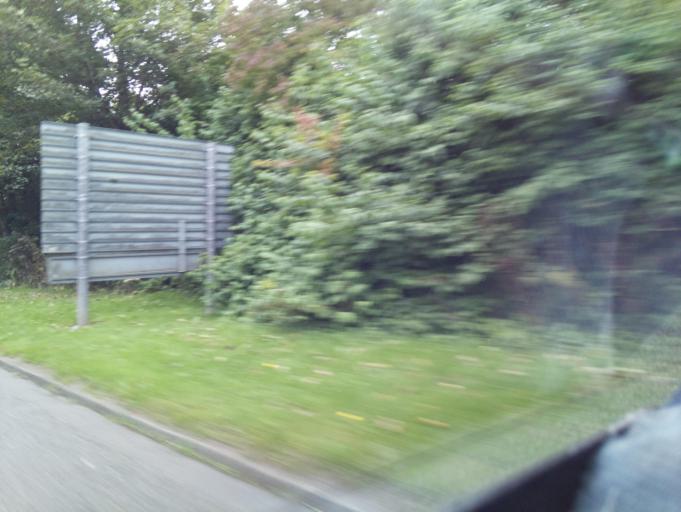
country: GB
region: Scotland
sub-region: Fife
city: Glenrothes
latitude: 56.2040
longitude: -3.1870
